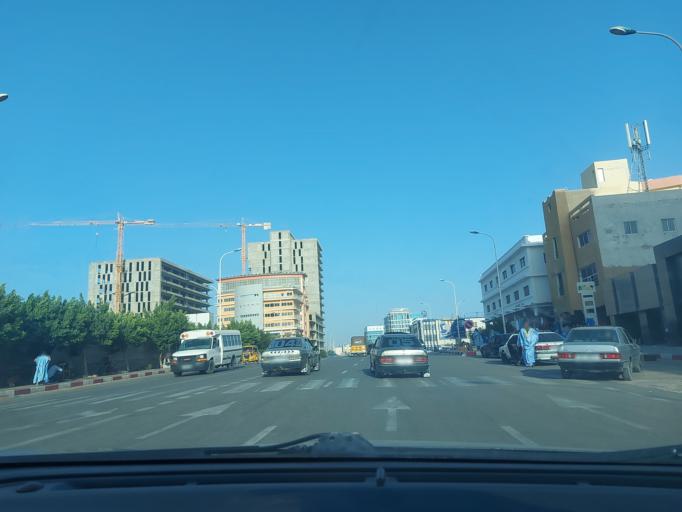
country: MR
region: Nouakchott
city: Nouakchott
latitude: 18.0876
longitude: -15.9753
